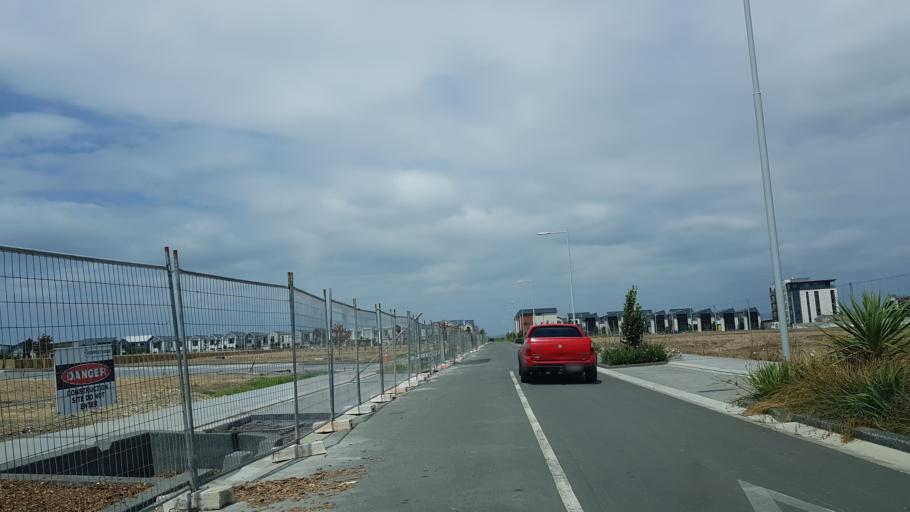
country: NZ
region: Auckland
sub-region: Auckland
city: Rosebank
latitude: -36.7896
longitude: 174.6648
